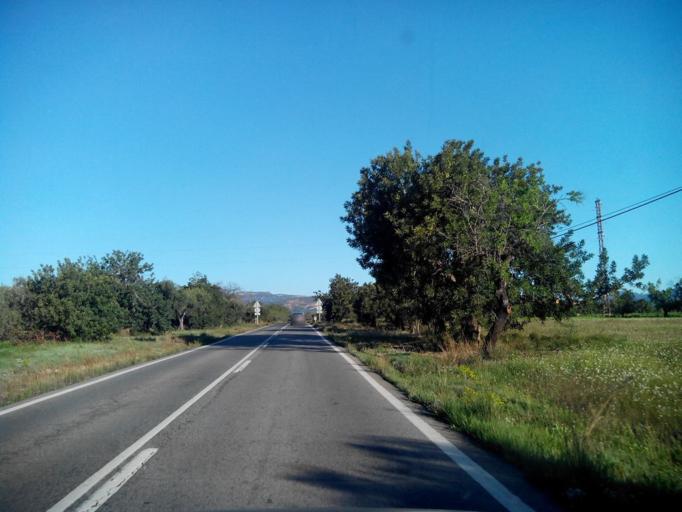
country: ES
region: Catalonia
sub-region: Provincia de Tarragona
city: Cambrils
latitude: 41.0644
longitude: 0.9884
